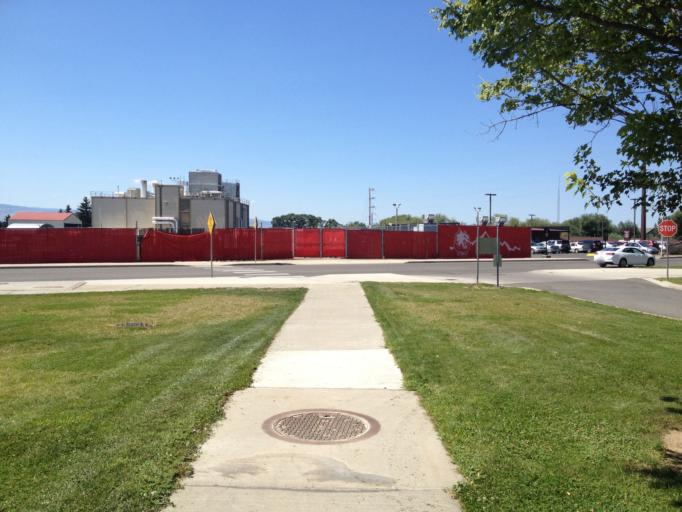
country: US
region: Washington
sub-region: Kittitas County
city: Ellensburg
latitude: 47.0038
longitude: -120.5428
